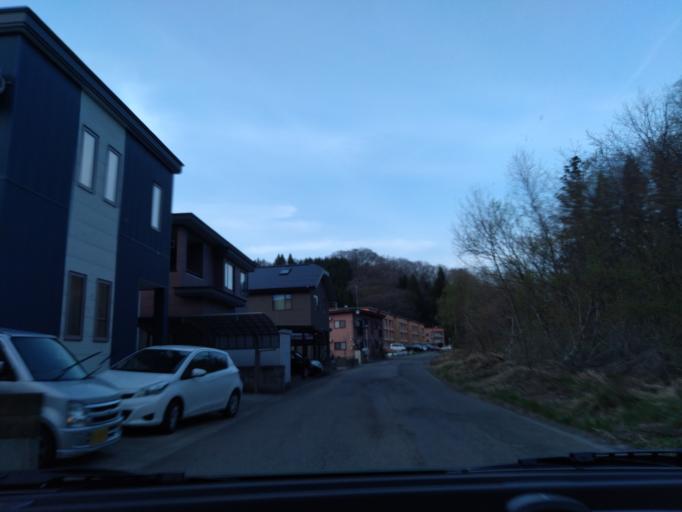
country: JP
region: Akita
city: Kakunodatemachi
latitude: 39.5924
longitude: 140.5791
